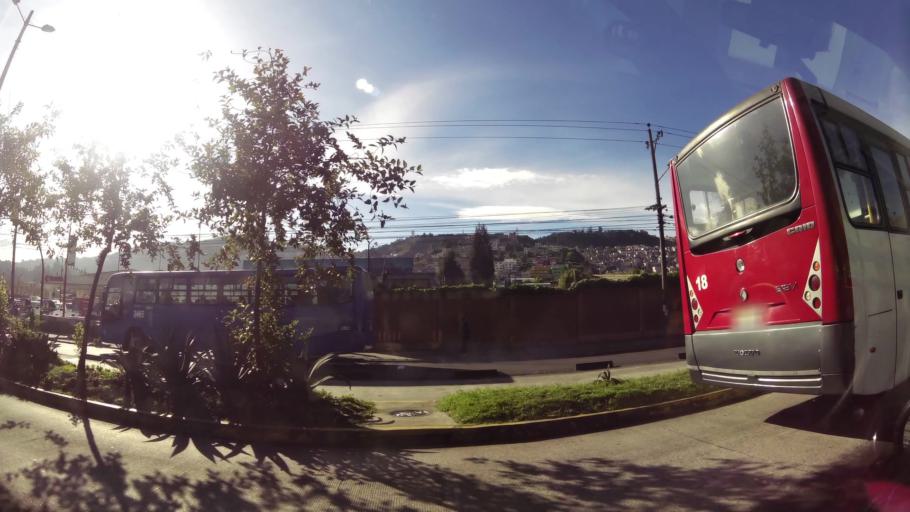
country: EC
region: Pichincha
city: Quito
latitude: -0.2723
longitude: -78.5292
